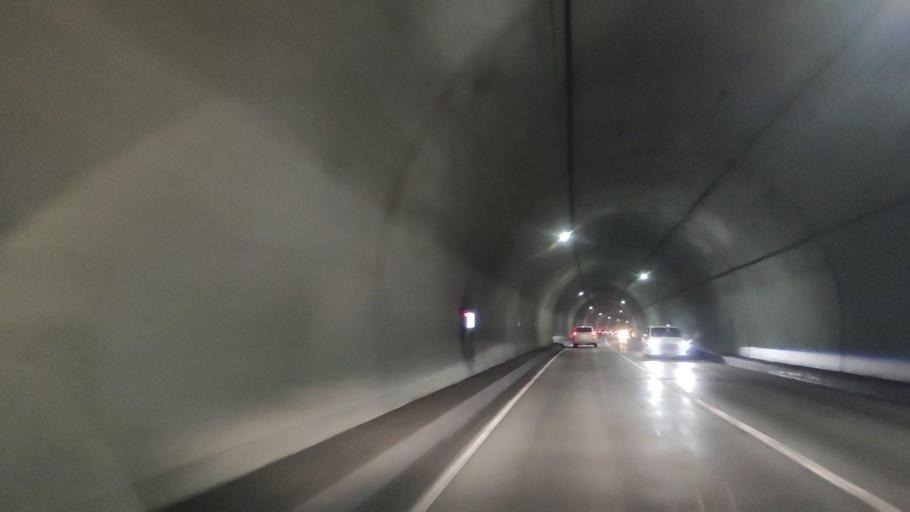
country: JP
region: Hokkaido
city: Ishikari
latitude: 43.5230
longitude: 141.3930
